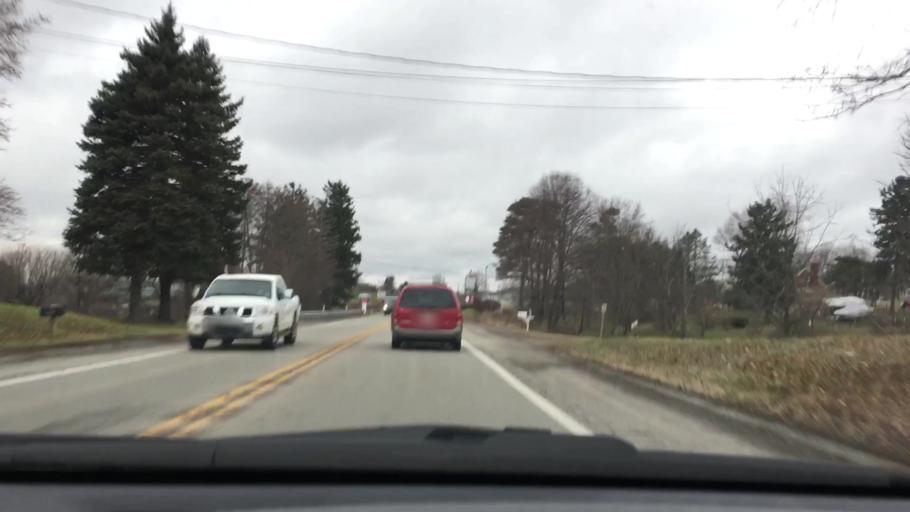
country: US
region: Pennsylvania
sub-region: Fayette County
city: South Uniontown
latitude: 39.8925
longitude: -79.8100
